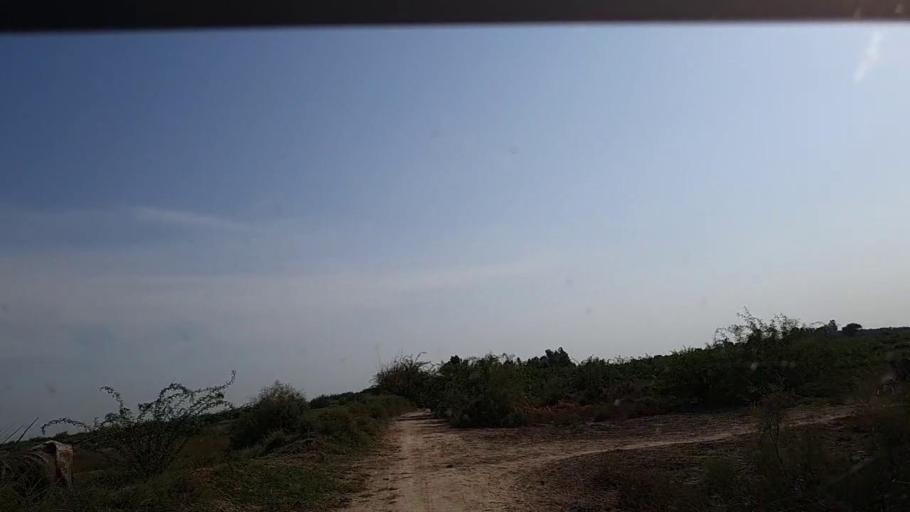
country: PK
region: Sindh
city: Adilpur
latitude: 27.9051
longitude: 69.2341
